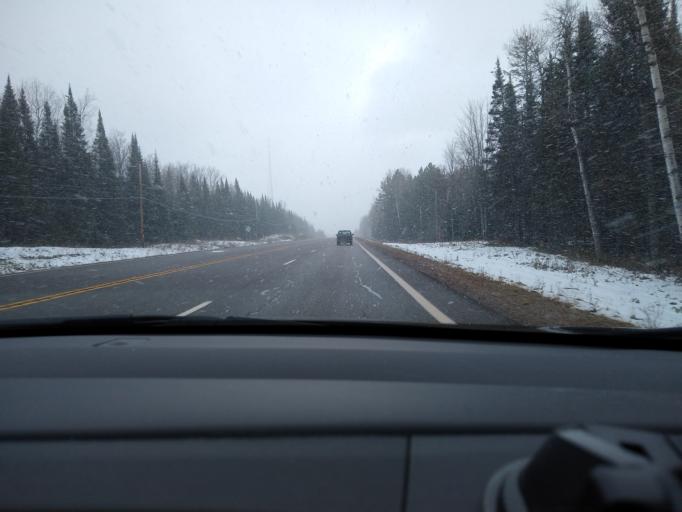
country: US
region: Wisconsin
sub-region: Florence County
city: Florence
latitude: 46.0492
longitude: -88.0626
